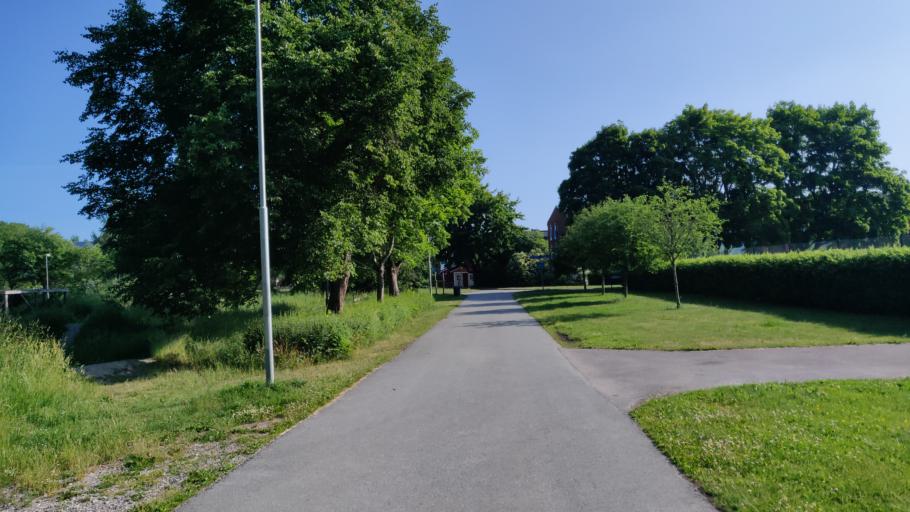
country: SE
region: OErebro
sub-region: Orebro Kommun
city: Orebro
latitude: 59.2880
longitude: 15.1663
